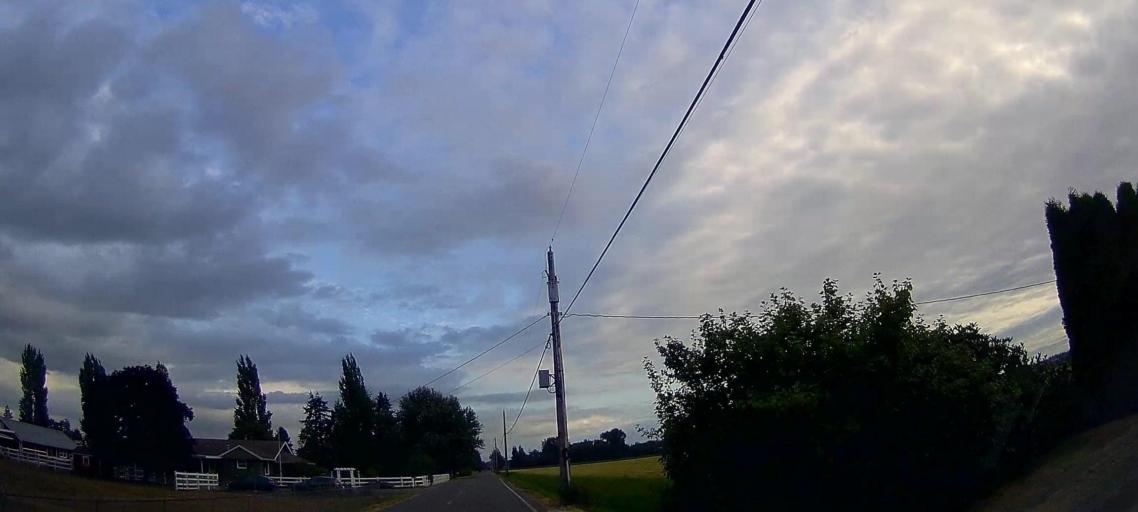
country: US
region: Washington
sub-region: Skagit County
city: Burlington
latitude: 48.5396
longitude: -122.4114
